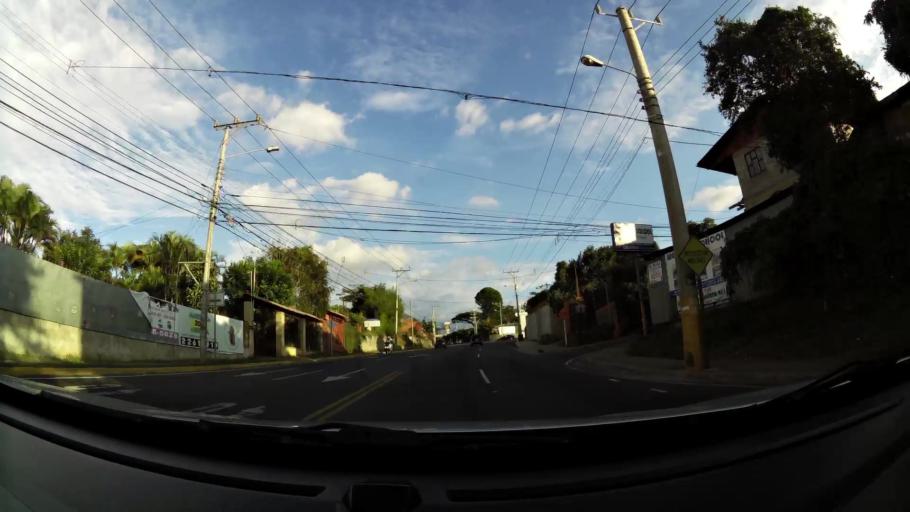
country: CR
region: Heredia
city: Llorente
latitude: 9.9998
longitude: -84.1465
